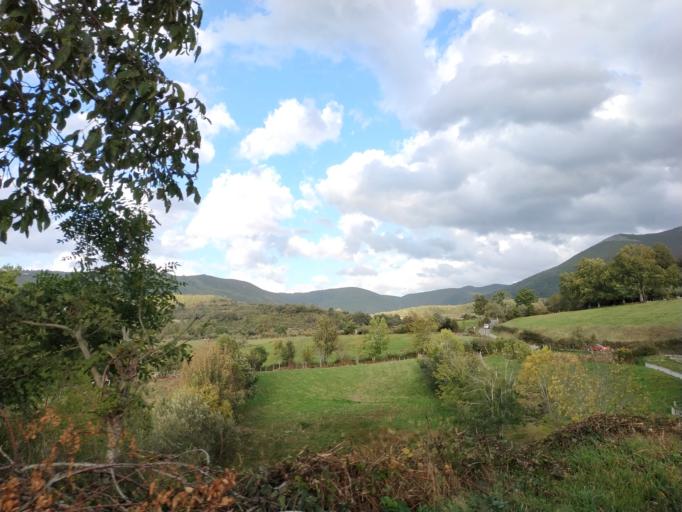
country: ES
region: Castille and Leon
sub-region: Provincia de Leon
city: Candin
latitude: 42.8574
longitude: -6.8755
